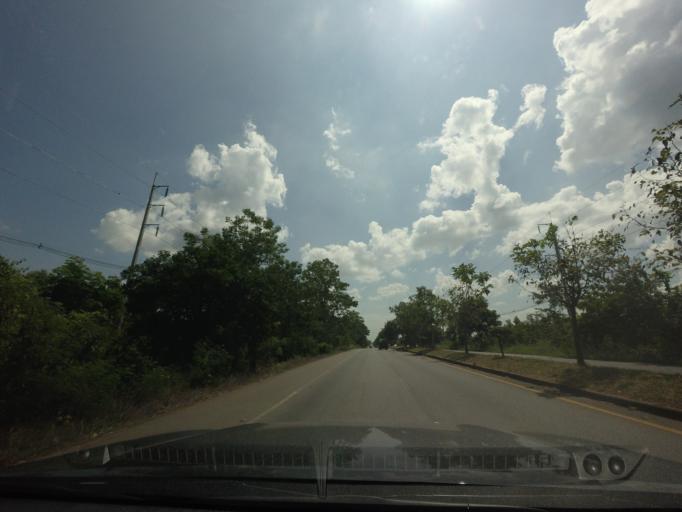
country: TH
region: Phetchabun
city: Nong Phai
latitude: 16.0291
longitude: 101.0759
